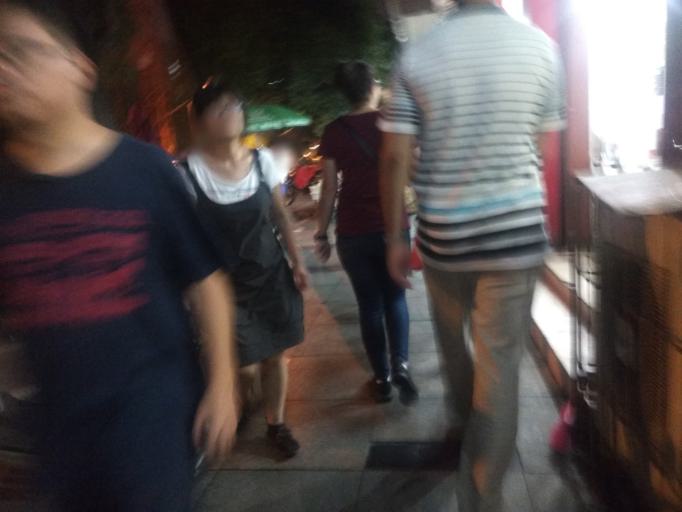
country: CN
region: Sichuan
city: Chengdu
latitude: 30.6613
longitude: 104.0666
